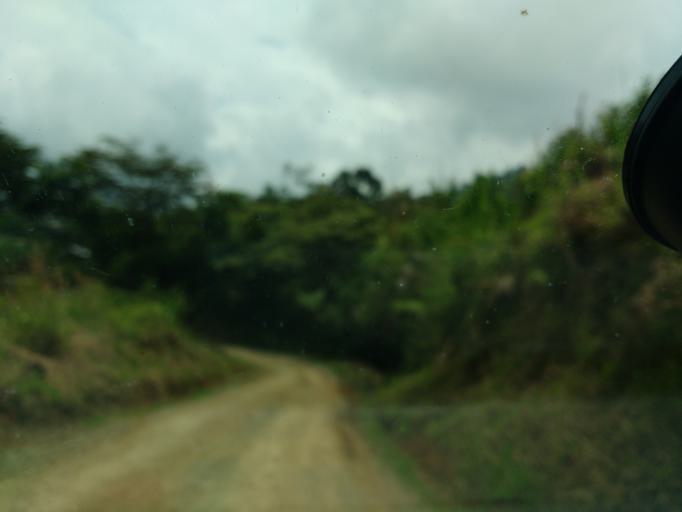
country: CO
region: Cauca
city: Santander de Quilichao
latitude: 2.9221
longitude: -76.4670
